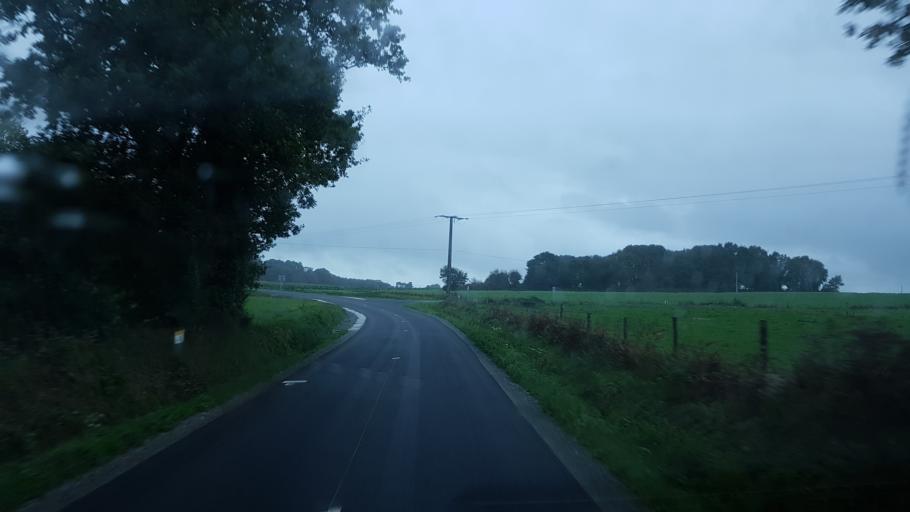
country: FR
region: Brittany
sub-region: Departement du Morbihan
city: Theix
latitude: 47.6530
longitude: -2.6303
